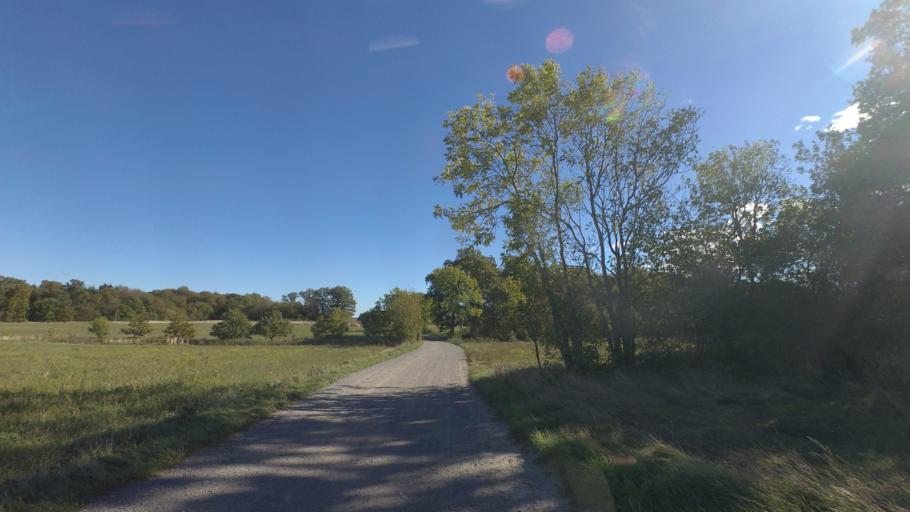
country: DK
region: Capital Region
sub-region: Bornholm Kommune
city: Nexo
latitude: 55.1203
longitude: 15.0576
